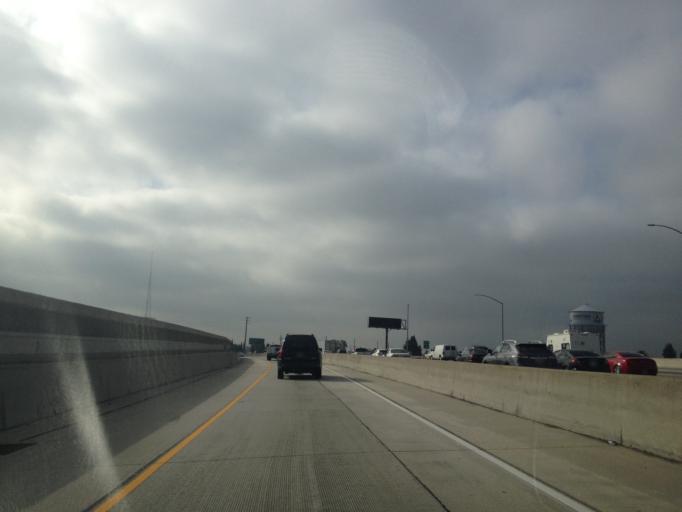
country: US
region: California
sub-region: Orange County
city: Santa Ana
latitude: 33.7608
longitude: -117.8631
